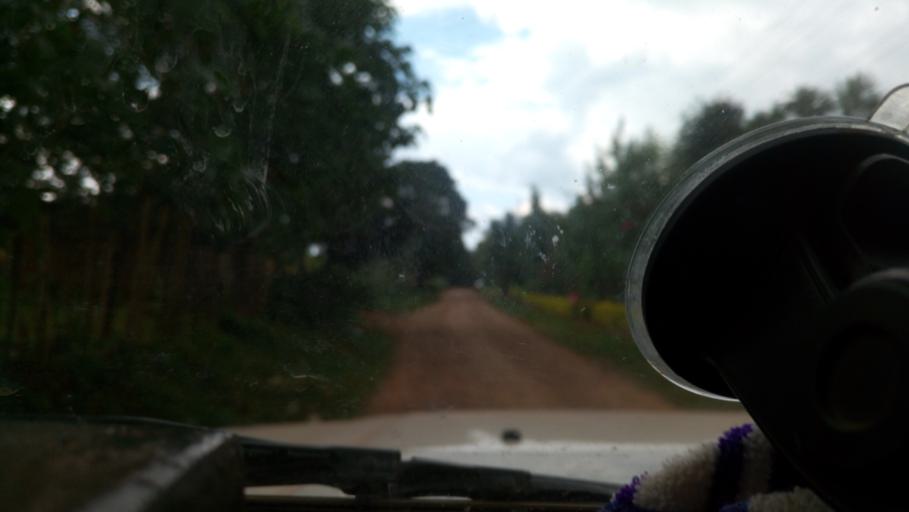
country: KE
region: Kericho
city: Litein
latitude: -0.6013
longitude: 35.1173
